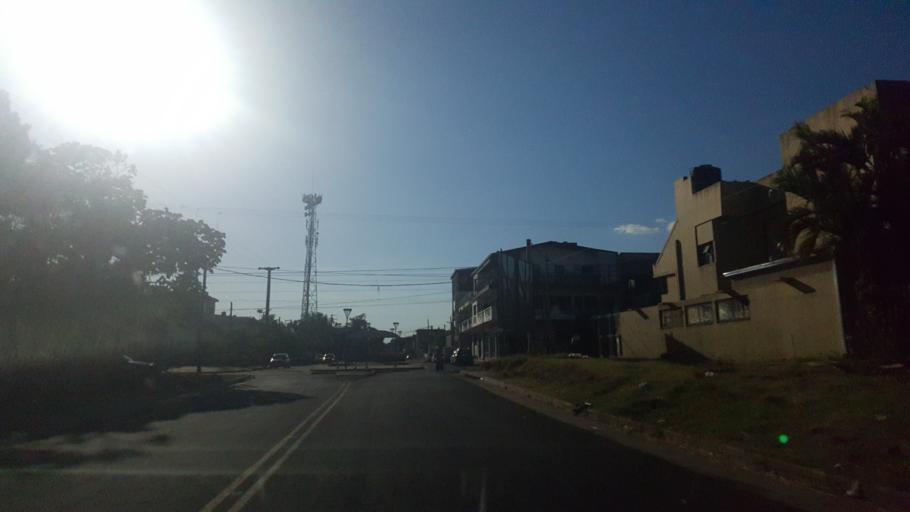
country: AR
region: Misiones
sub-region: Departamento de Capital
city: Posadas
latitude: -27.3814
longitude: -55.8951
